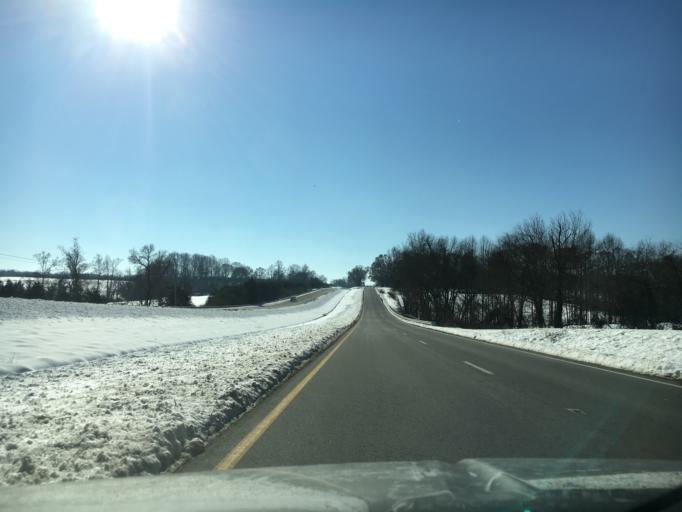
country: US
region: Virginia
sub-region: Nottoway County
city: Crewe
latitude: 37.2696
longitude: -78.1273
